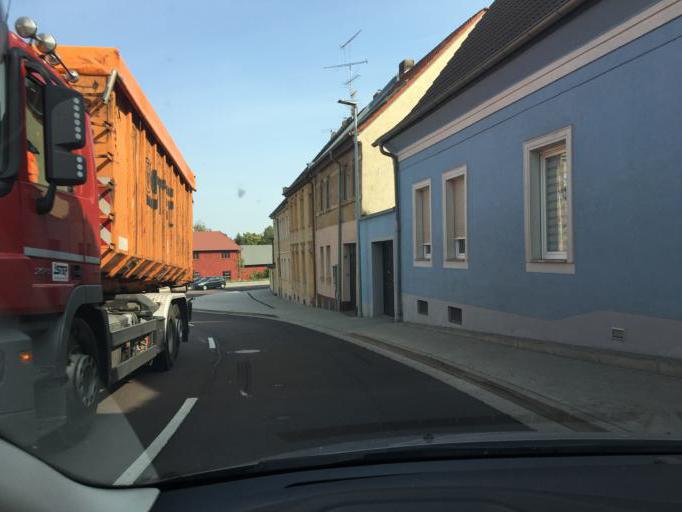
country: DE
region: Saxony-Anhalt
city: Nienburg/Saale
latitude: 51.8401
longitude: 11.7699
